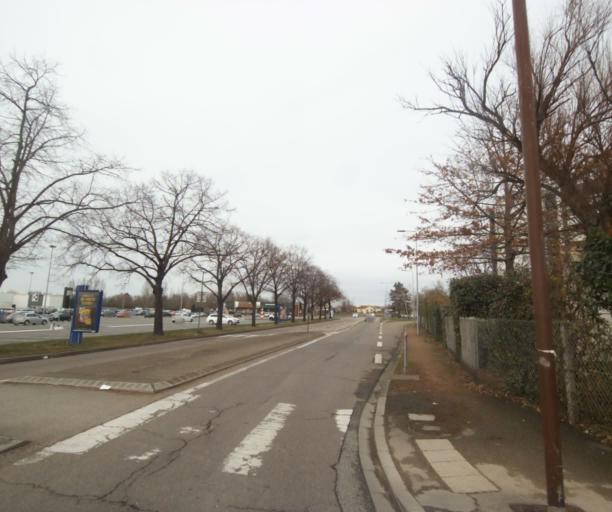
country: FR
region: Rhone-Alpes
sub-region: Departement de la Loire
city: Riorges
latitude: 46.0440
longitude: 4.0548
